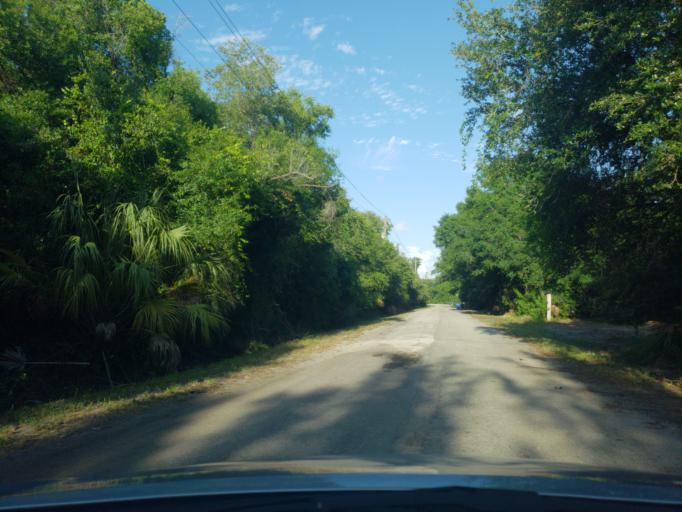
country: US
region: Florida
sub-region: Hillsborough County
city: Progress Village
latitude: 27.9045
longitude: -82.3502
